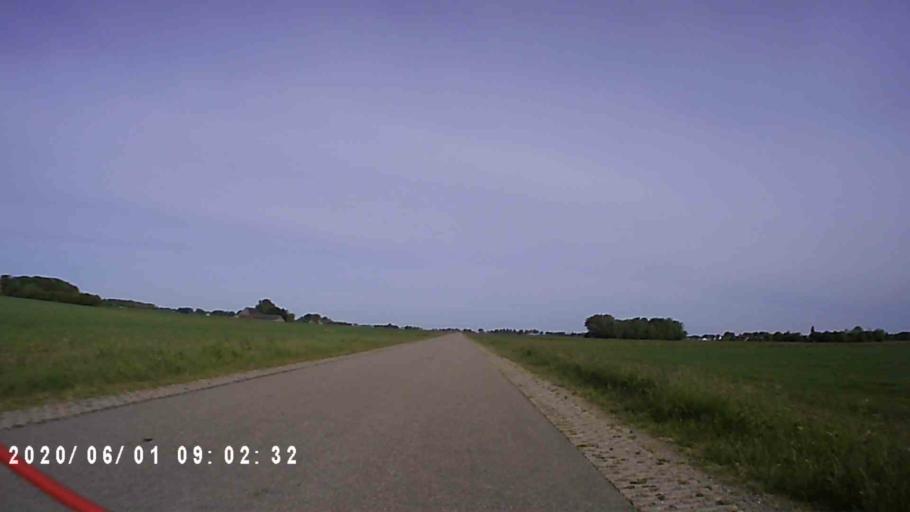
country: NL
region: Friesland
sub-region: Gemeente Ferwerderadiel
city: Hallum
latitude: 53.2928
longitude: 5.7859
